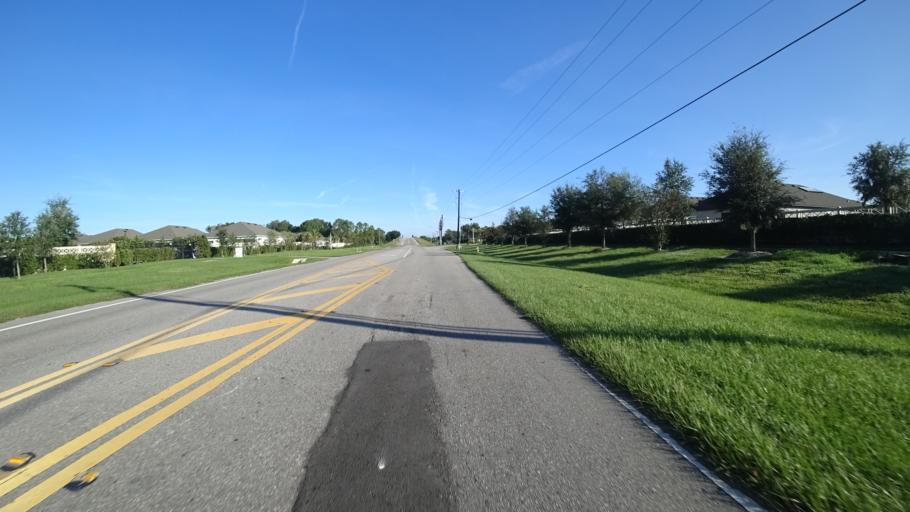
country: US
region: Florida
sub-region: Manatee County
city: Memphis
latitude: 27.5812
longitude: -82.5274
